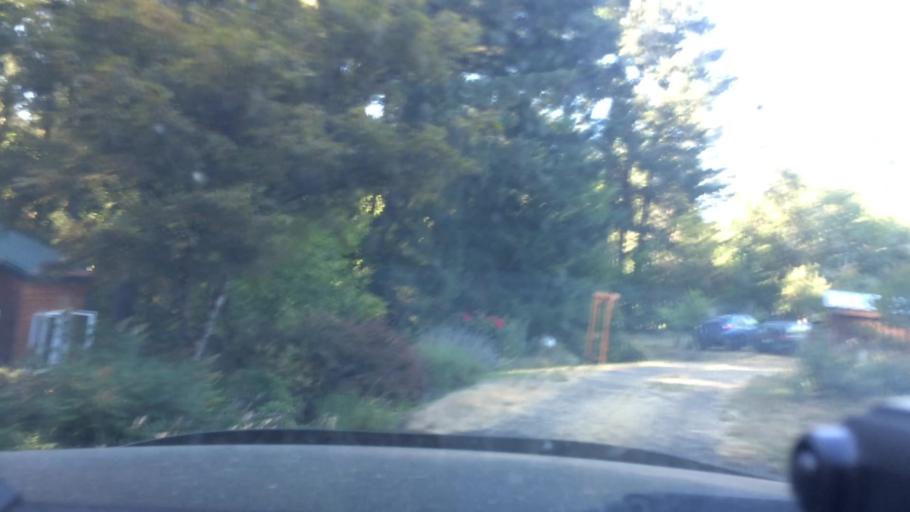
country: US
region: Oregon
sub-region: Yamhill County
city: Newberg
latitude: 45.3759
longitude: -122.9763
